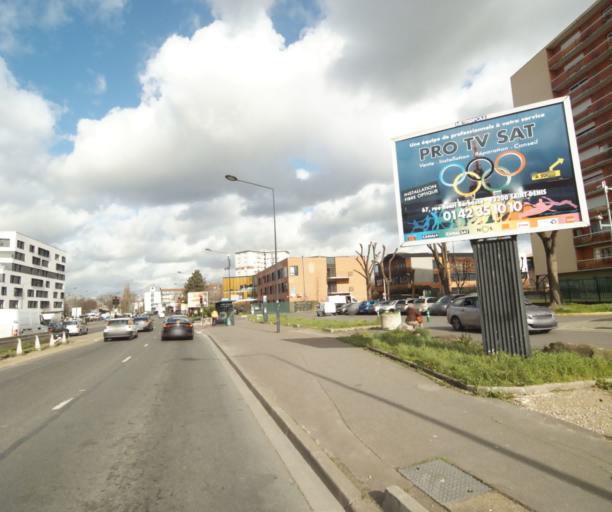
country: FR
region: Ile-de-France
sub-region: Departement de Seine-Saint-Denis
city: Saint-Denis
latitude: 48.9357
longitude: 2.3724
